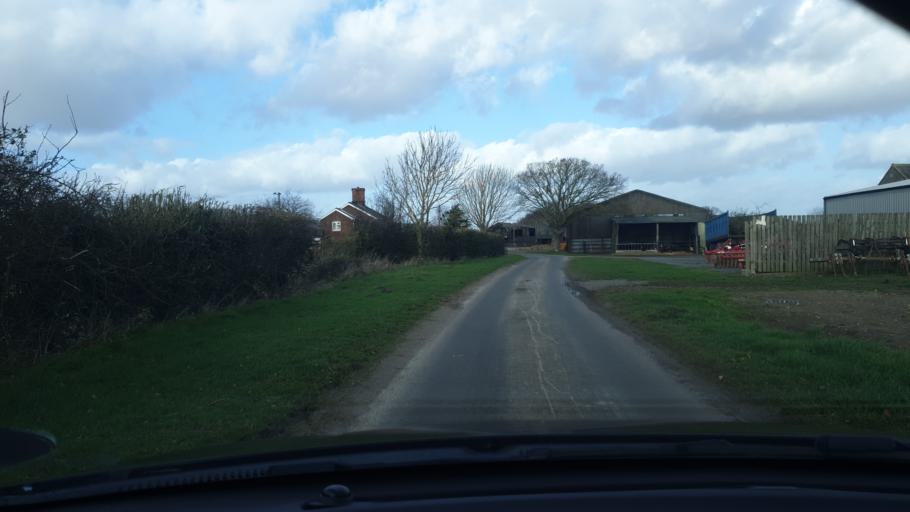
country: GB
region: England
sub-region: Essex
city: Manningtree
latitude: 51.9293
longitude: 1.0606
